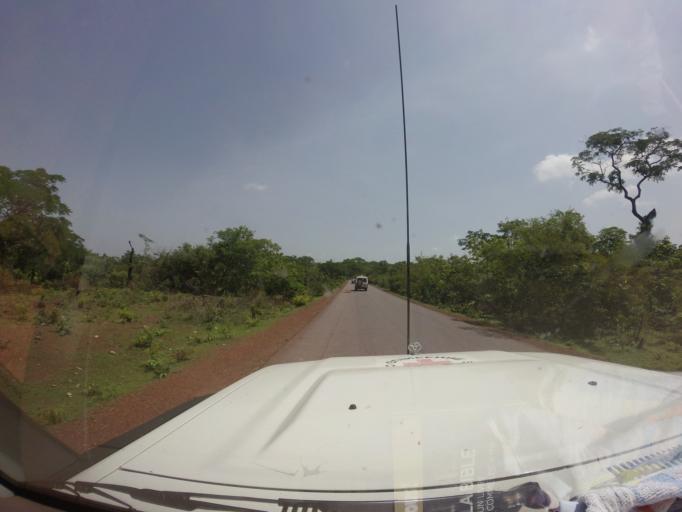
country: GN
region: Mamou
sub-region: Mamou Prefecture
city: Mamou
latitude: 10.2949
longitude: -12.3652
